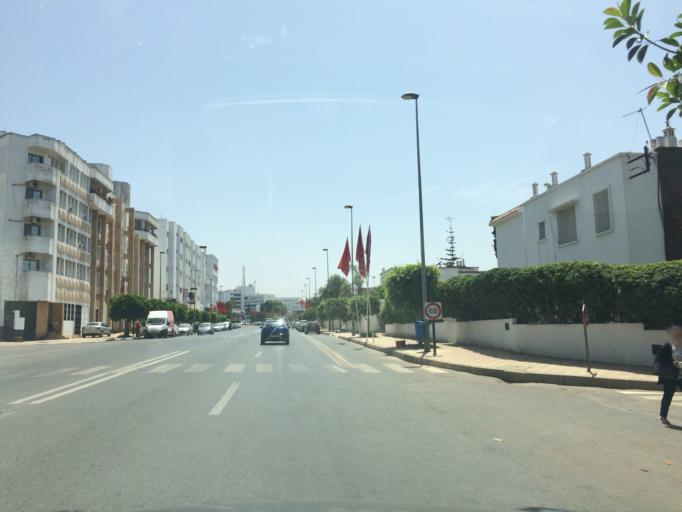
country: MA
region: Rabat-Sale-Zemmour-Zaer
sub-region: Rabat
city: Rabat
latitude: 33.9893
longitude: -6.8515
